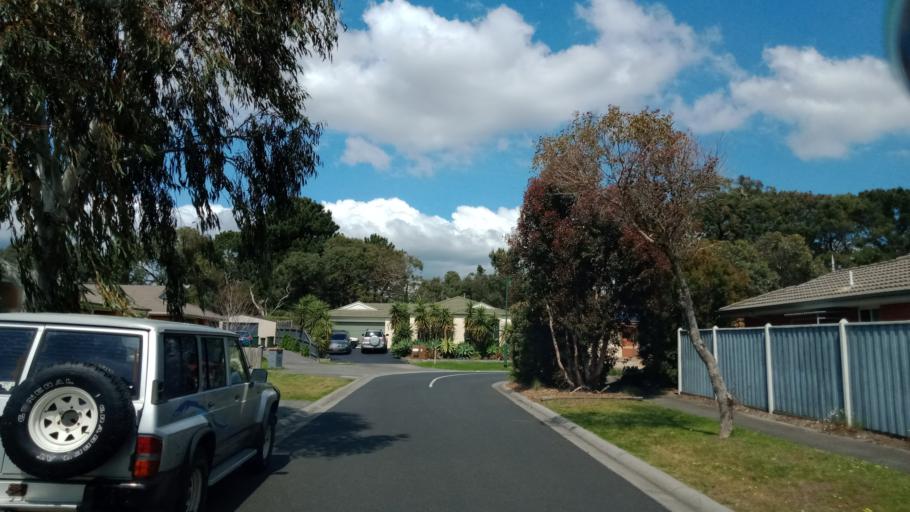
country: AU
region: Victoria
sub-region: Frankston
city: Carrum Downs
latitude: -38.0952
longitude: 145.1925
